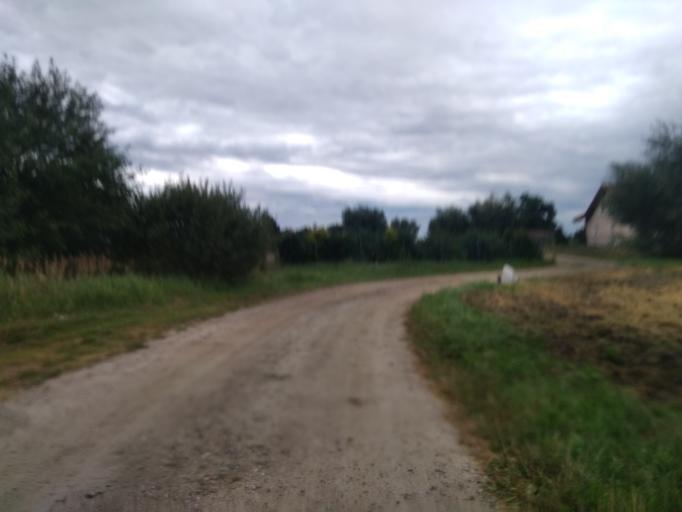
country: PL
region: Kujawsko-Pomorskie
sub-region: Powiat bydgoski
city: Osielsko
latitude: 53.2263
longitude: 18.1453
